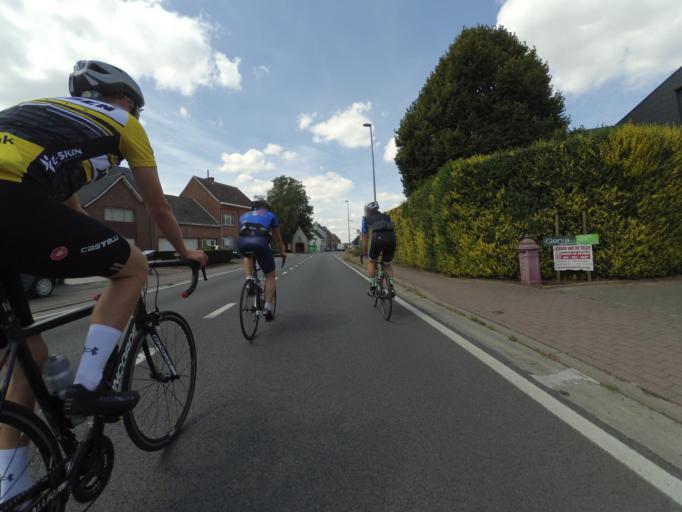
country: BE
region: Flanders
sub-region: Provincie Oost-Vlaanderen
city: Zottegem
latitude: 50.8671
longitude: 3.8006
